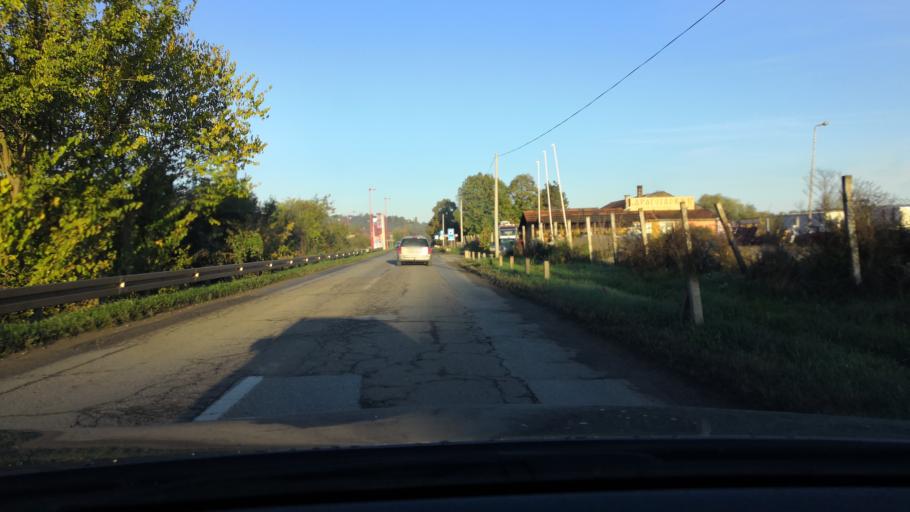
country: RS
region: Autonomna Pokrajina Vojvodina
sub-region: Juznobacki Okrug
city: Sremski Karlovci
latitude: 45.2070
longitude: 19.9308
